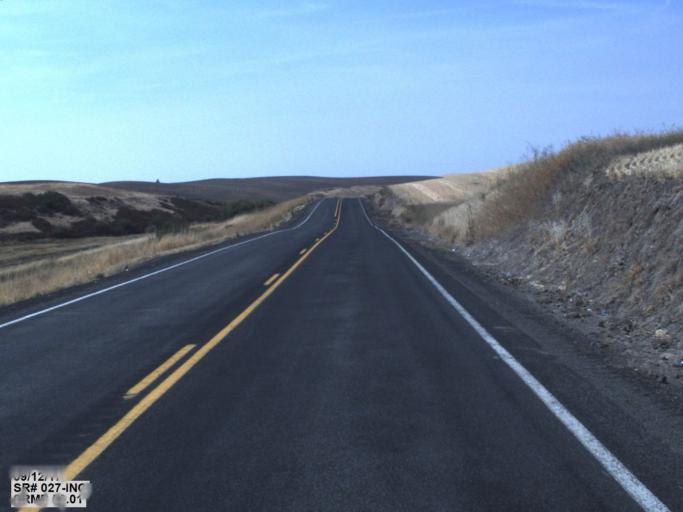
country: US
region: Idaho
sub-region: Benewah County
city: Plummer
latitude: 47.2319
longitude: -117.1012
